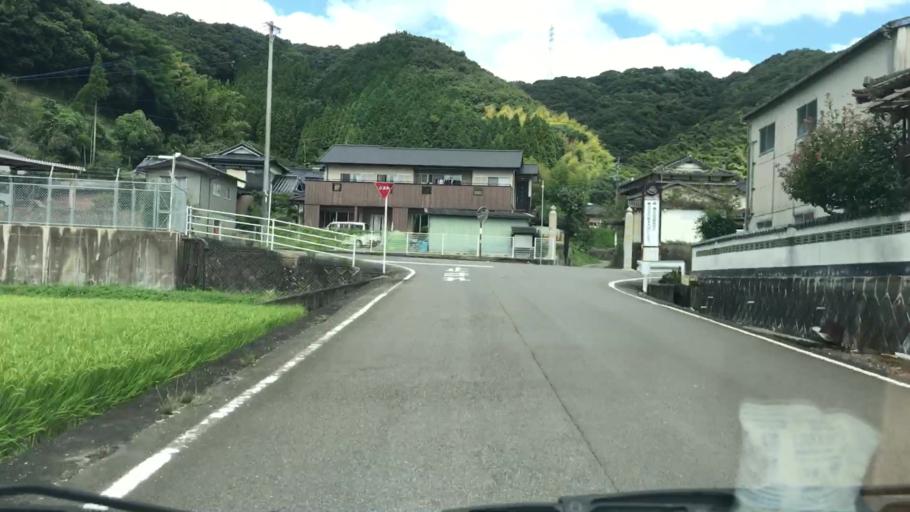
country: JP
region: Saga Prefecture
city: Takeocho-takeo
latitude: 33.2326
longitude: 130.1508
